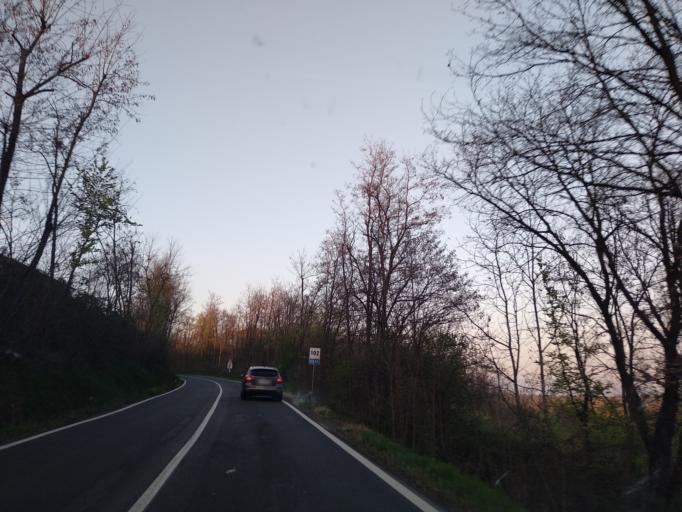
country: IT
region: Emilia-Romagna
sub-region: Provincia di Reggio Emilia
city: Puianello
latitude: 44.6286
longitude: 10.5688
